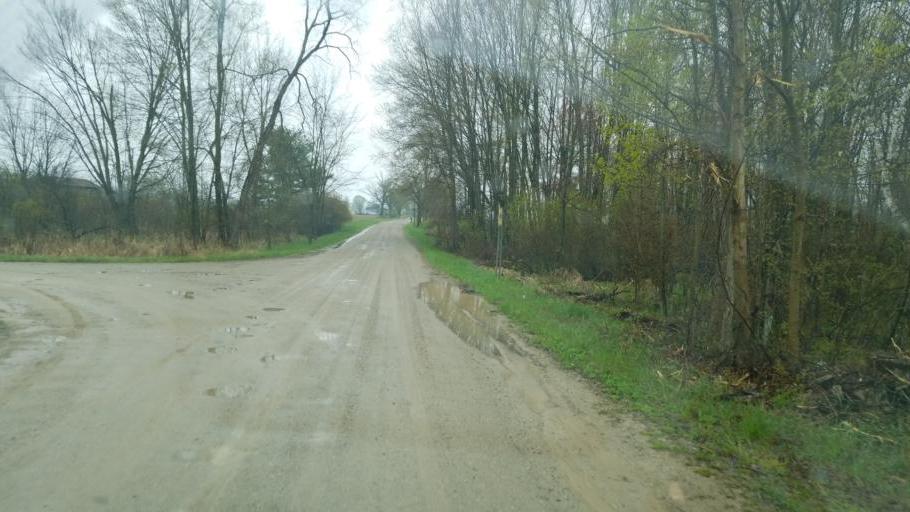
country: US
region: Michigan
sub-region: Montcalm County
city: Lakeview
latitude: 43.4682
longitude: -85.3332
